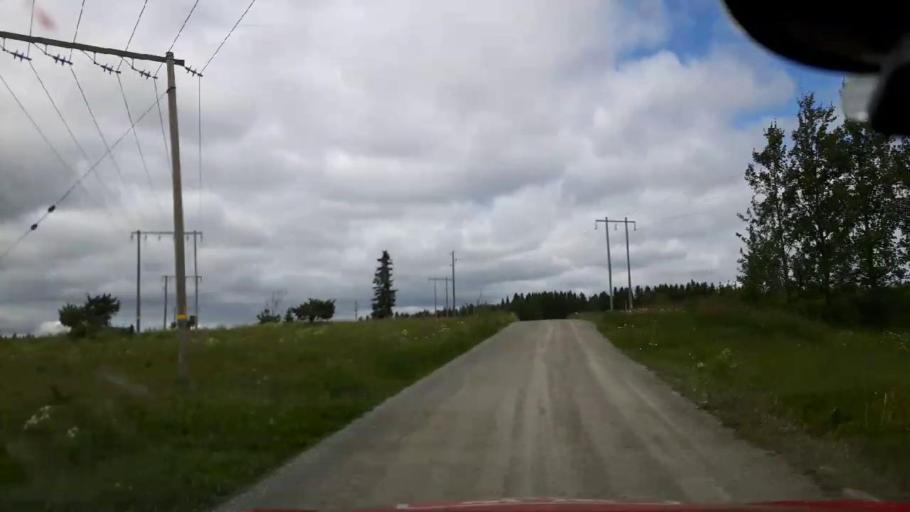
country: SE
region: Jaemtland
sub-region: OEstersunds Kommun
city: Brunflo
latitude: 63.0927
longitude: 14.8234
